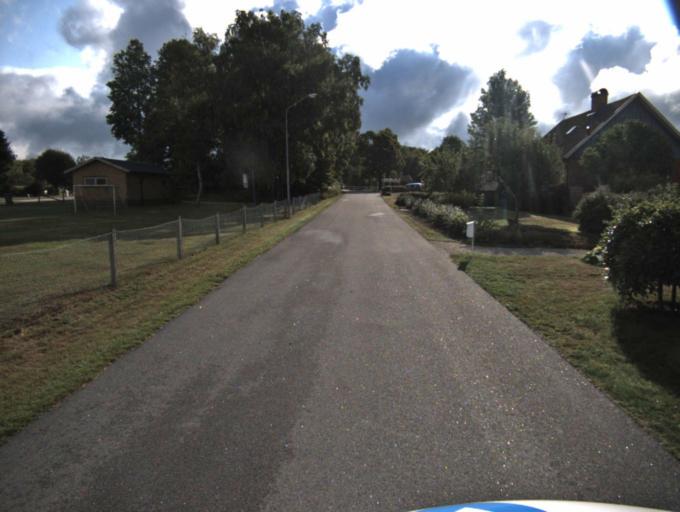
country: SE
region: Vaestra Goetaland
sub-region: Ulricehamns Kommun
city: Ulricehamn
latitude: 57.6767
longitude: 13.4707
